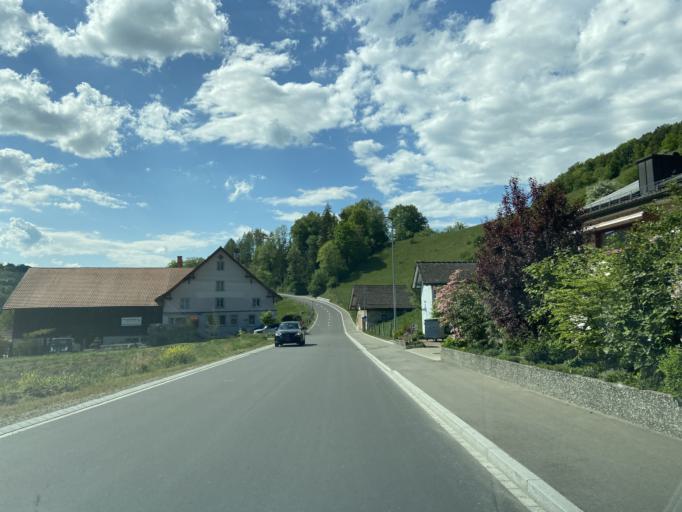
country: CH
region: Zurich
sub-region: Bezirk Winterthur
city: Pfungen
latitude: 47.5213
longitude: 8.6354
